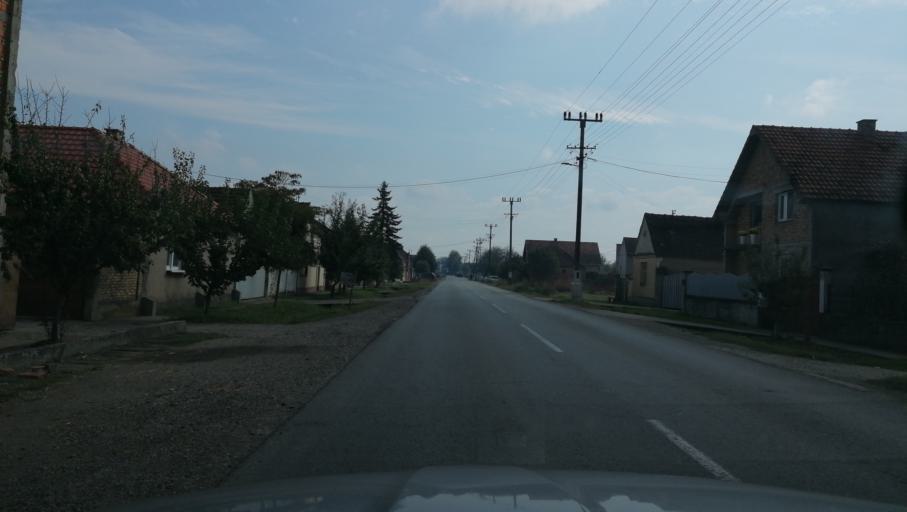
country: RS
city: Ravnje
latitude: 45.0272
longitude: 19.3942
